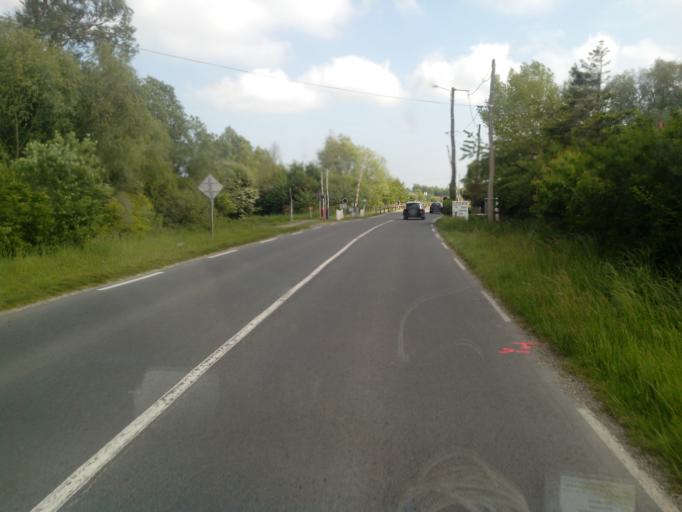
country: FR
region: Picardie
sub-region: Departement de la Somme
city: Saint-Valery-sur-Somme
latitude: 50.1934
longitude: 1.6988
